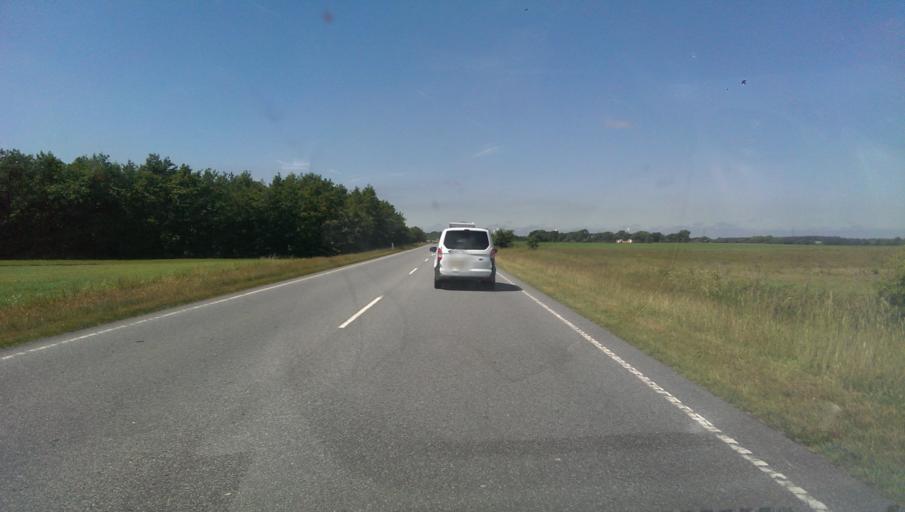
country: DK
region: South Denmark
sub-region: Esbjerg Kommune
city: Esbjerg
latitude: 55.5324
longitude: 8.4265
